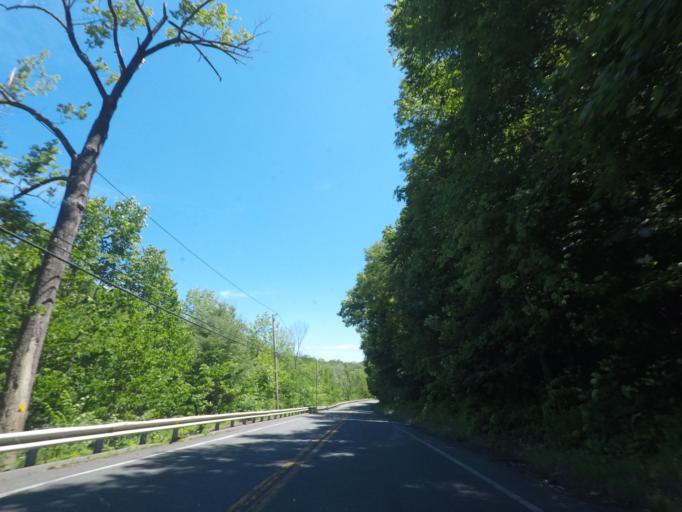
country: US
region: Massachusetts
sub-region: Berkshire County
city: Becket
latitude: 42.2622
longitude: -72.9614
